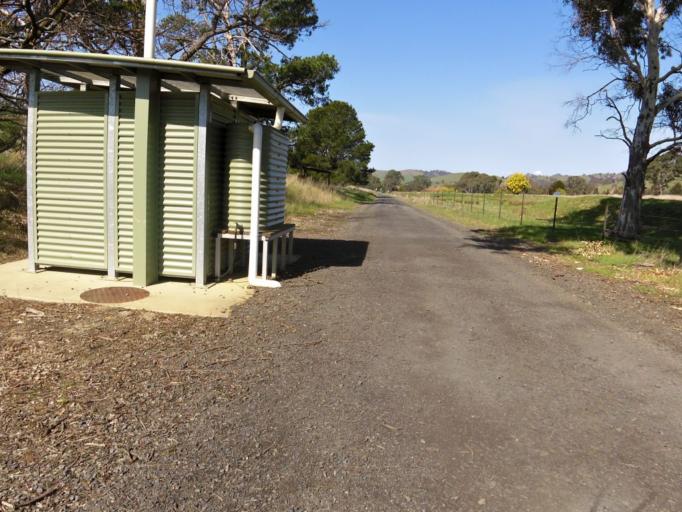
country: AU
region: Victoria
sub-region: Murrindindi
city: Alexandra
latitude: -37.0185
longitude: 145.8004
